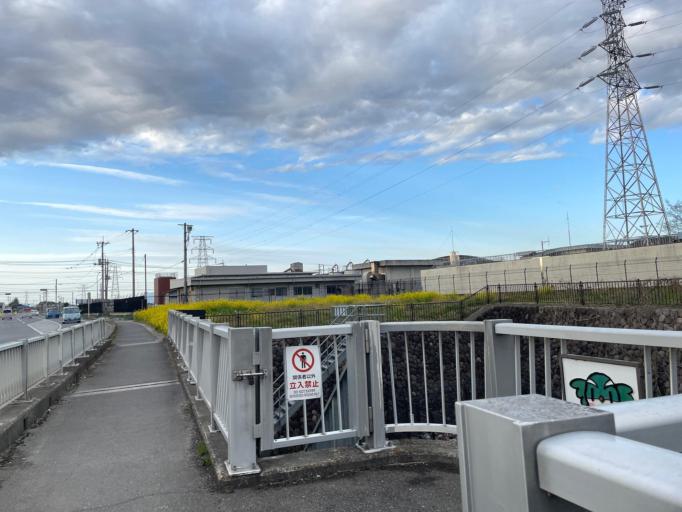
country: JP
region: Saitama
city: Fukayacho
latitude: 36.1339
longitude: 139.2658
